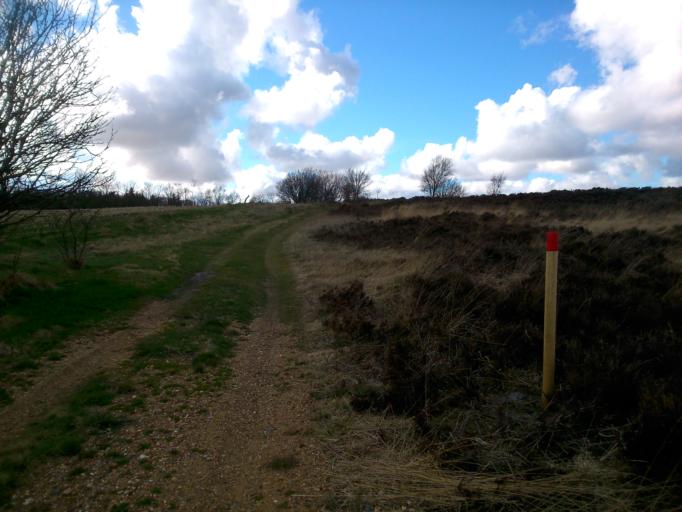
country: DK
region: Central Jutland
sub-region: Ringkobing-Skjern Kommune
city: Ringkobing
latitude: 56.1365
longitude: 8.3686
